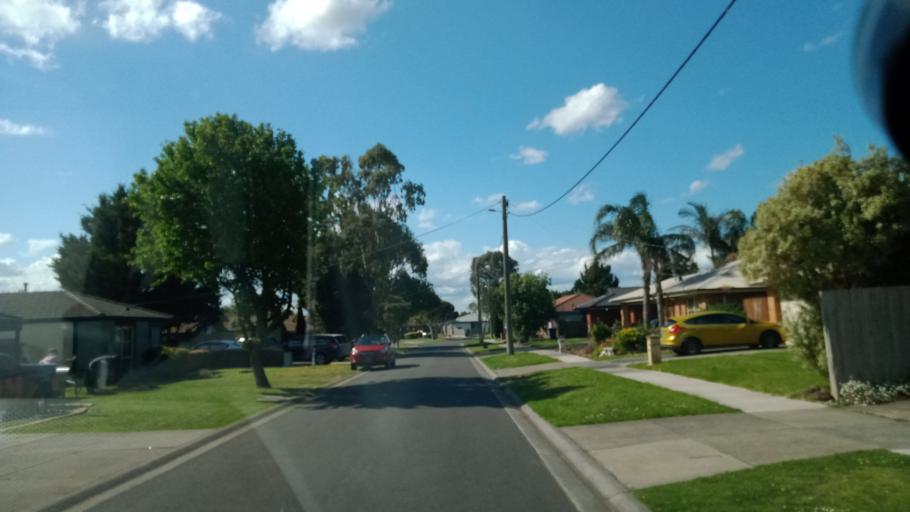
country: AU
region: Victoria
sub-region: Casey
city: Cranbourne West
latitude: -38.1041
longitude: 145.2604
